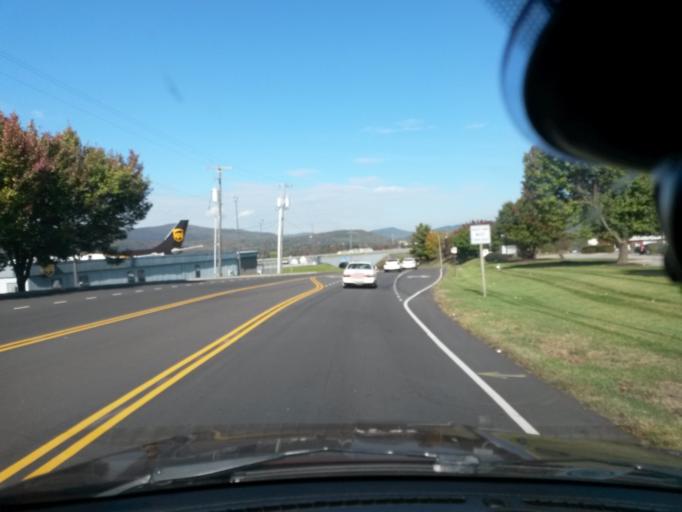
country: US
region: Virginia
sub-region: Roanoke County
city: Hollins
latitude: 37.3295
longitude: -79.9674
